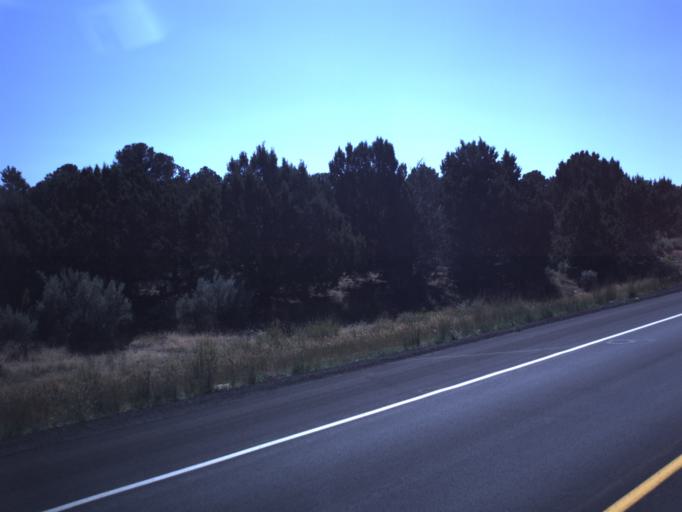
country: US
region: Utah
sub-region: Utah County
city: Eagle Mountain
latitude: 40.0075
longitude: -112.2761
